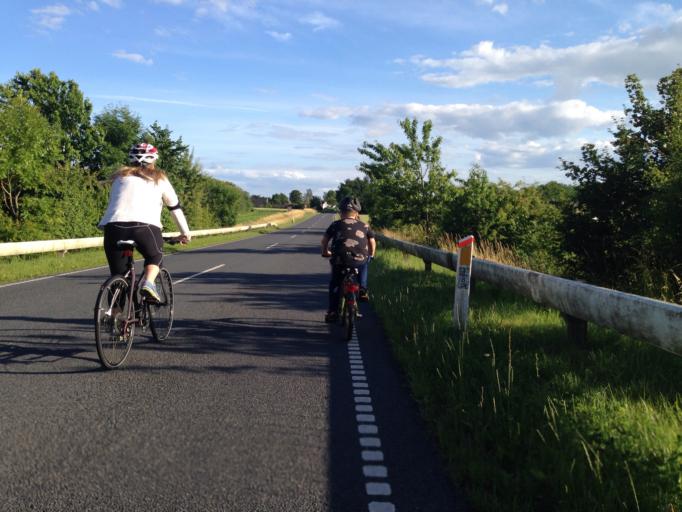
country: DK
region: South Denmark
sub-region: Middelfart Kommune
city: Norre Aby
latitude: 55.4850
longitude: 9.9022
